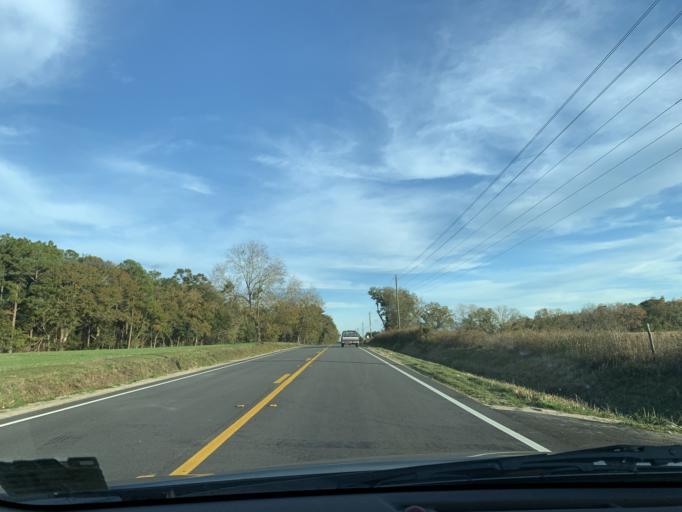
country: US
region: Georgia
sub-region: Irwin County
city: Ocilla
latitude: 31.5926
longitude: -83.1031
